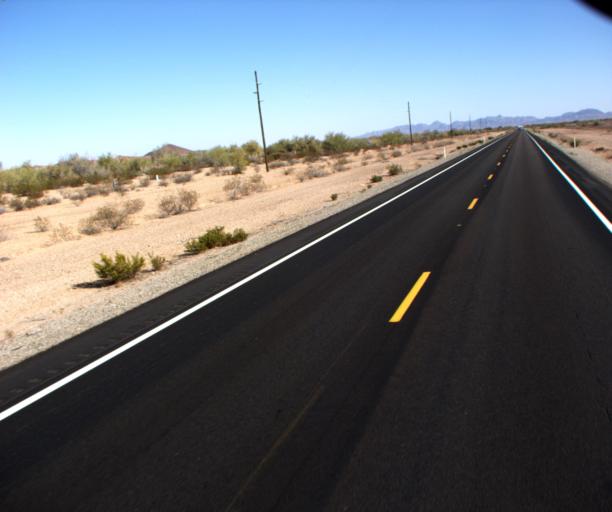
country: US
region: Arizona
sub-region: Yuma County
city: Fortuna Foothills
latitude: 32.9552
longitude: -114.2968
